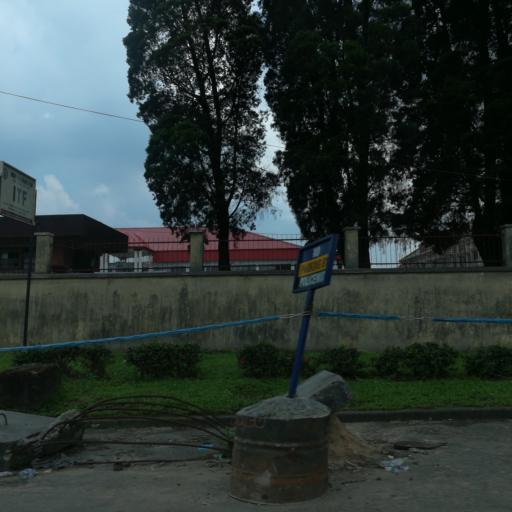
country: NG
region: Rivers
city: Port Harcourt
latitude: 4.8144
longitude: 7.0359
